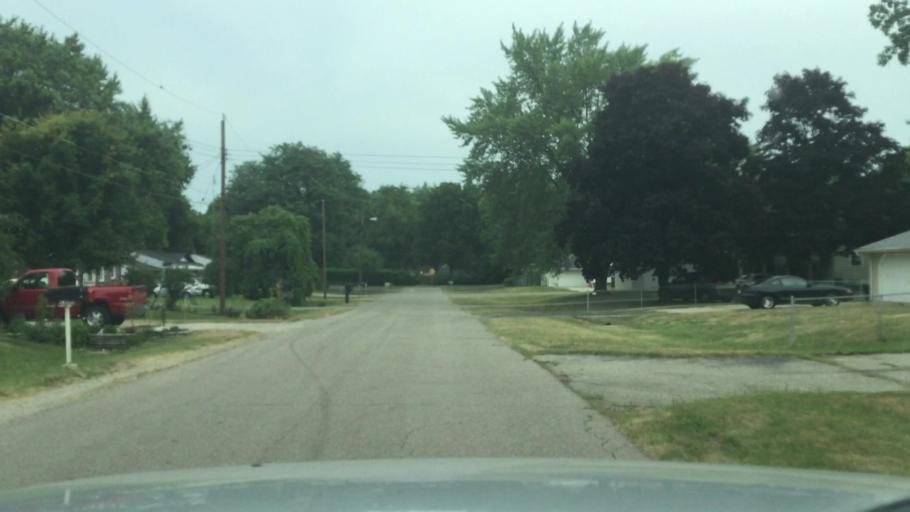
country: US
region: Michigan
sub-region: Genesee County
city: Flint
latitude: 42.9615
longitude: -83.7019
